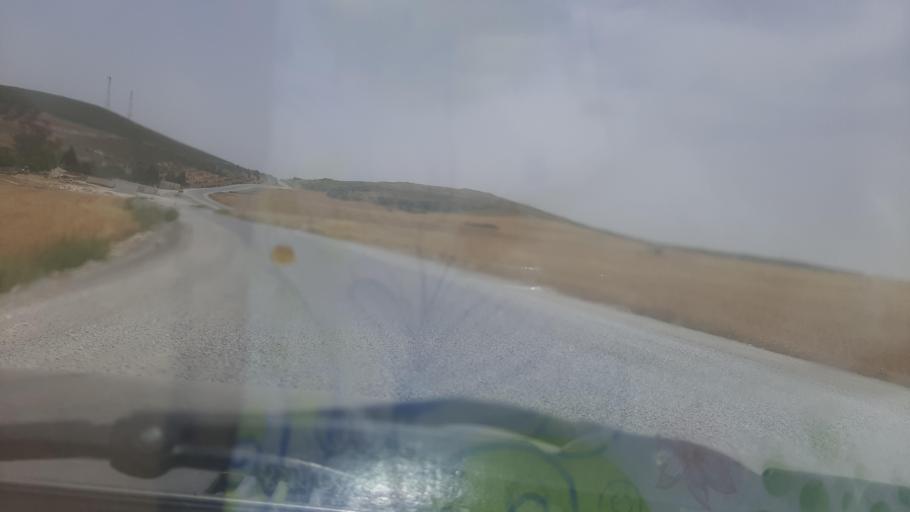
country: TN
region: Tunis
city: La Mohammedia
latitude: 36.5394
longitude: 10.1521
